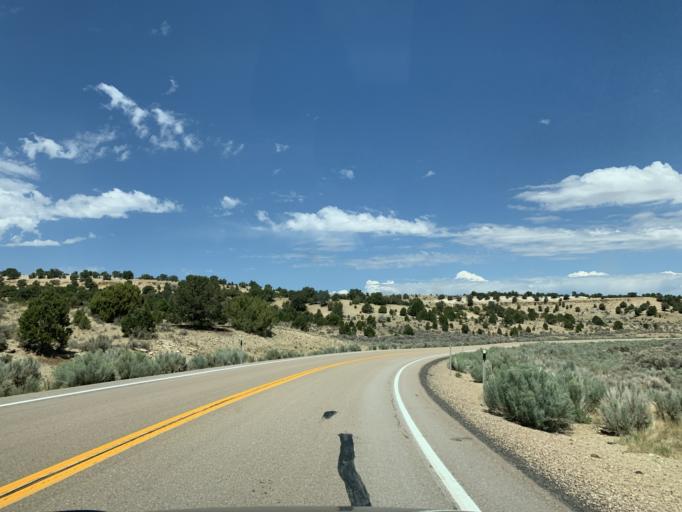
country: US
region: Utah
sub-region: Duchesne County
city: Duchesne
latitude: 39.9010
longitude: -110.2353
